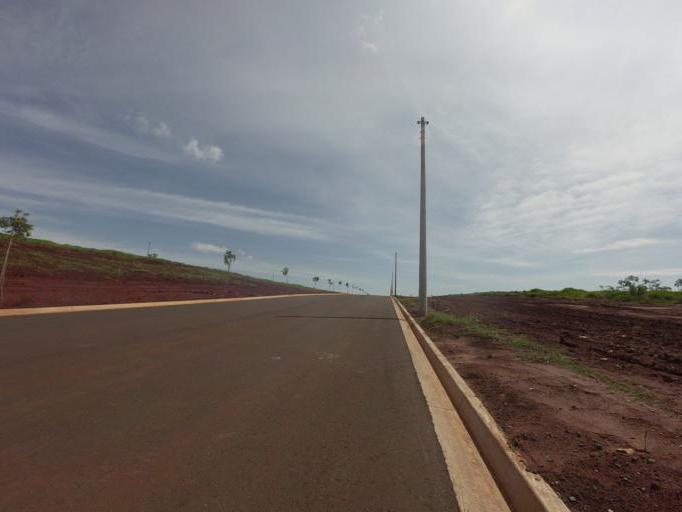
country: BR
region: Sao Paulo
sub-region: Piracicaba
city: Piracicaba
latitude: -22.7614
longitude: -47.5795
